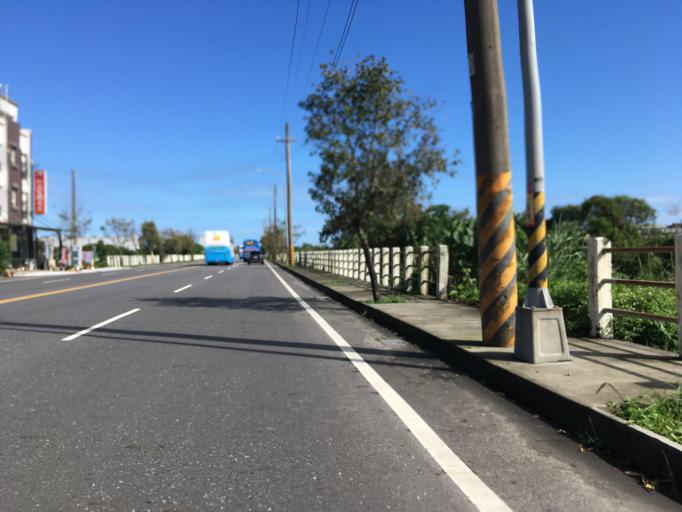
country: TW
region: Taiwan
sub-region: Yilan
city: Yilan
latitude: 24.6139
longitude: 121.8430
